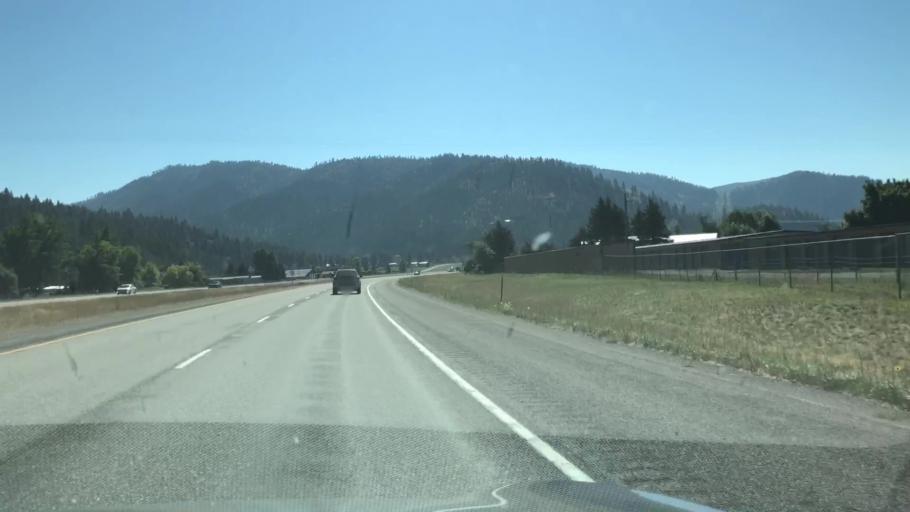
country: US
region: Montana
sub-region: Missoula County
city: Clinton
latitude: 46.7864
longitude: -113.7234
